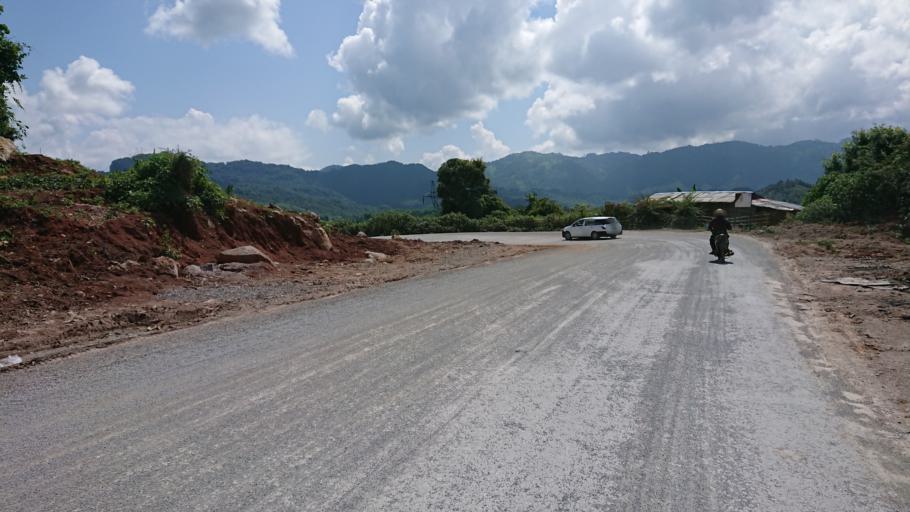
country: MM
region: Shan
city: Taunggyi
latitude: 20.8117
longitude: 97.3228
